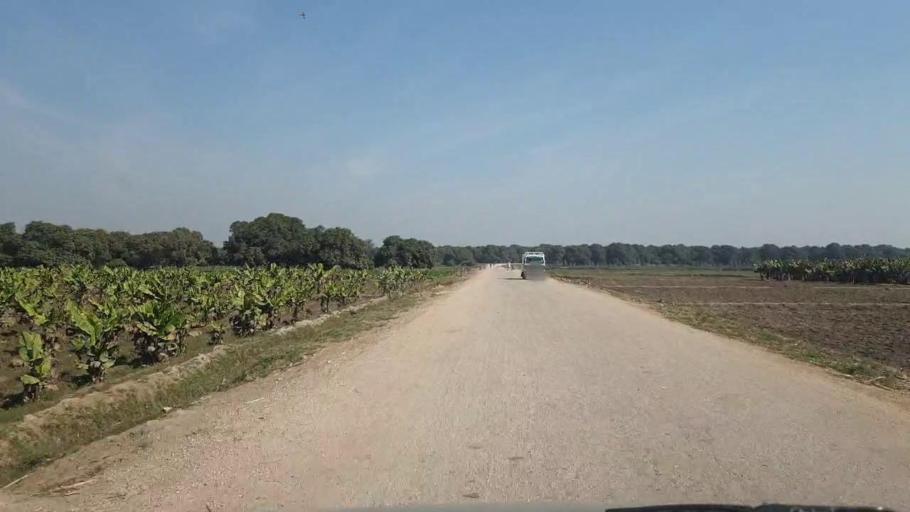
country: PK
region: Sindh
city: Tando Allahyar
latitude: 25.3989
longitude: 68.7721
